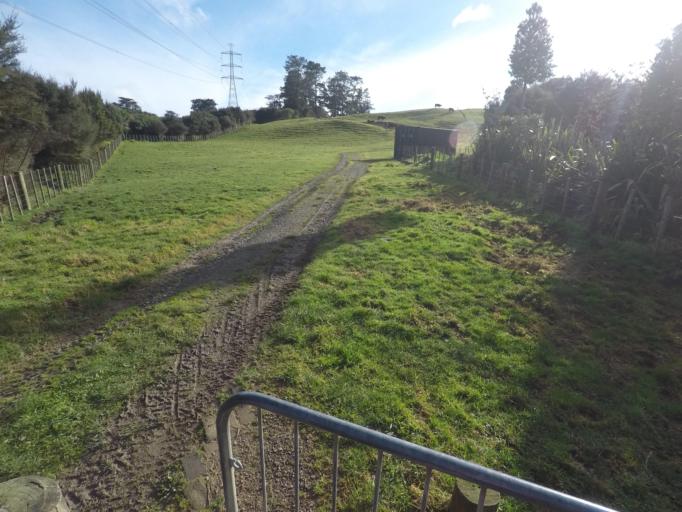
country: NZ
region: Auckland
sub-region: Auckland
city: Manukau City
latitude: -36.9928
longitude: 174.9099
